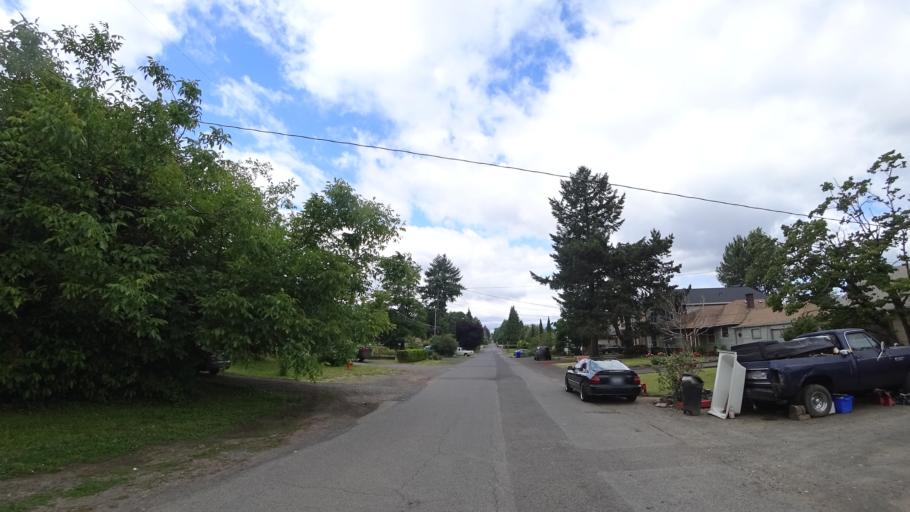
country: US
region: Oregon
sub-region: Multnomah County
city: Portland
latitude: 45.5664
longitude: -122.6025
